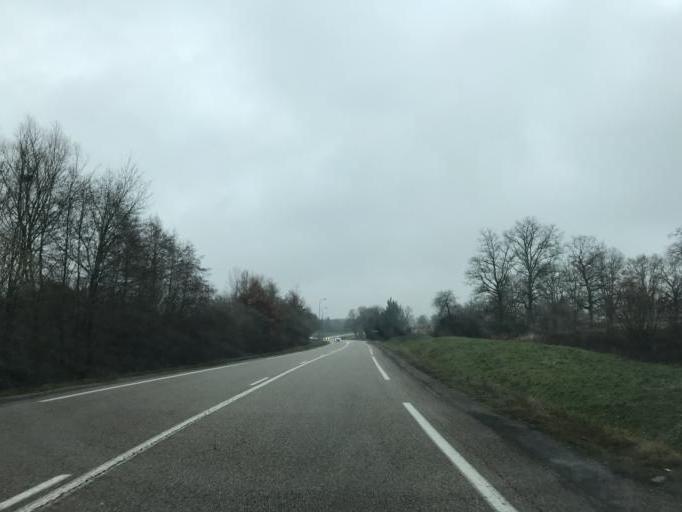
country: FR
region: Rhone-Alpes
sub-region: Departement de l'Ain
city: Peronnas
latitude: 46.1833
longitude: 5.1949
